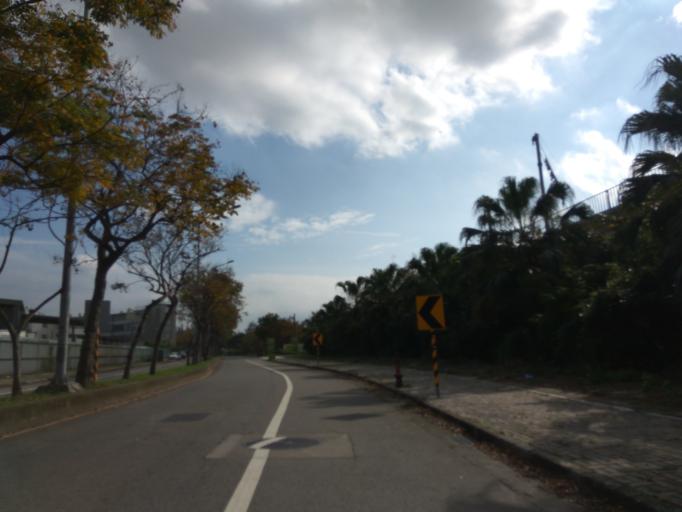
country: TW
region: Taiwan
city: Taoyuan City
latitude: 25.0576
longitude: 121.1799
